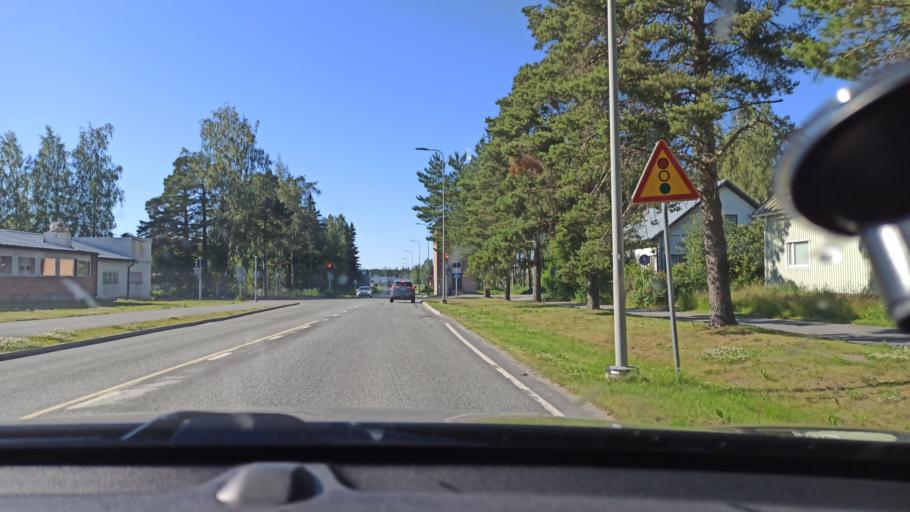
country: FI
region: Ostrobothnia
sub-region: Jakobstadsregionen
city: Jakobstad
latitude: 63.6836
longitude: 22.7133
